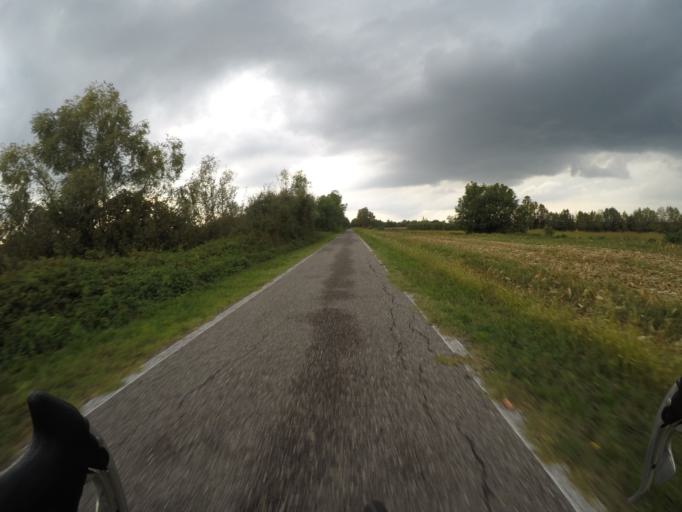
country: IT
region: Veneto
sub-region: Provincia di Rovigo
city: Frassinelle Polesine
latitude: 44.9955
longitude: 11.7068
